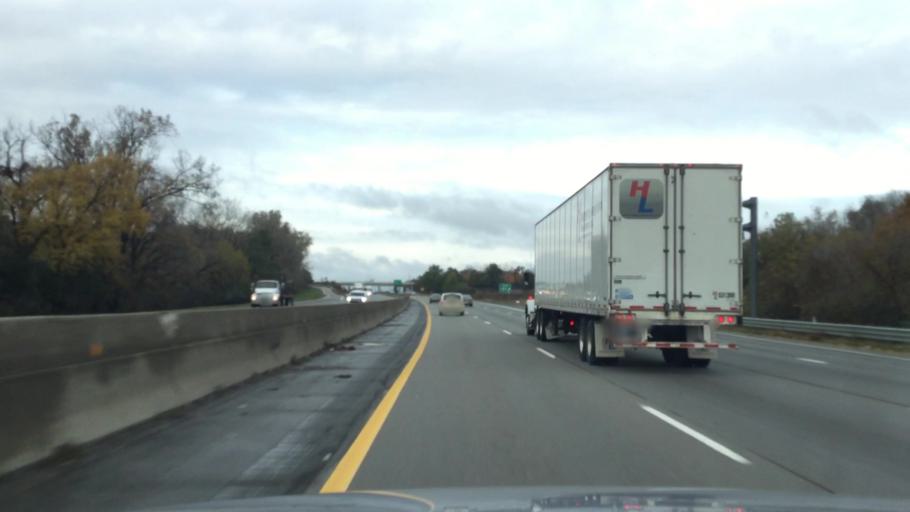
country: US
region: Michigan
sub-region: Washtenaw County
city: Ypsilanti
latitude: 42.2307
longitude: -83.6094
